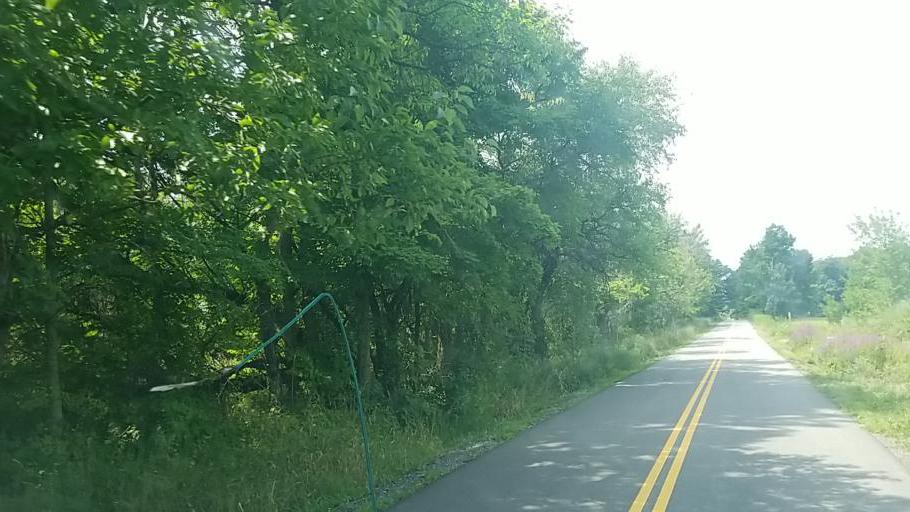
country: US
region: Ohio
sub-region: Medina County
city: Lodi
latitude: 41.1124
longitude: -82.0760
